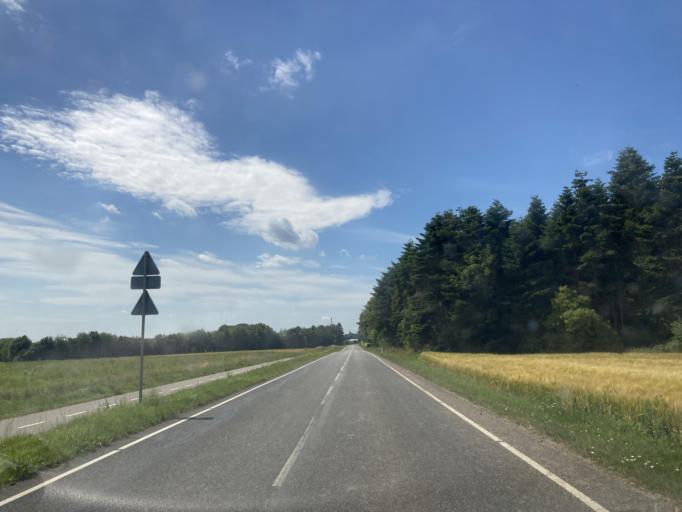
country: DK
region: Zealand
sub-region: Solrod Kommune
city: Solrod
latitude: 55.5211
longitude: 12.1594
